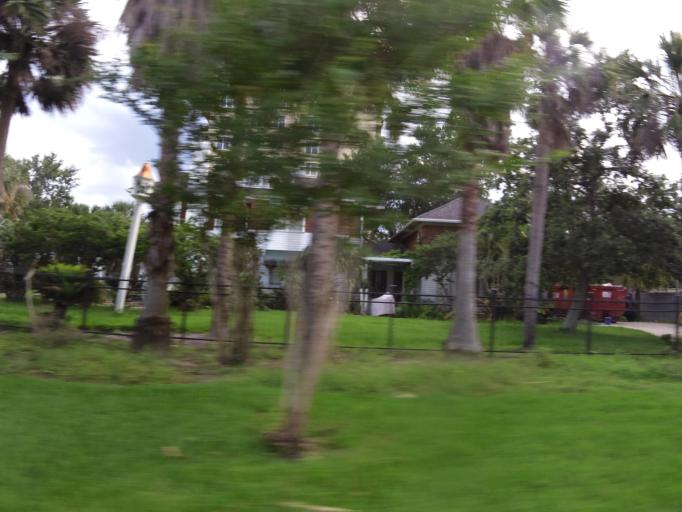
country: US
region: Florida
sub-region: Duval County
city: Jacksonville
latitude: 30.3089
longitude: -81.6856
